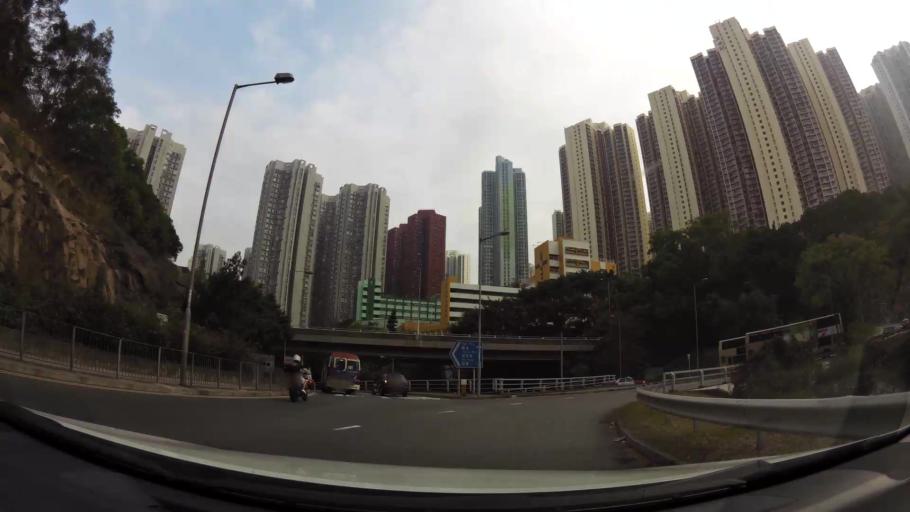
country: HK
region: Kowloon City
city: Kowloon
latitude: 22.3044
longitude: 114.2350
